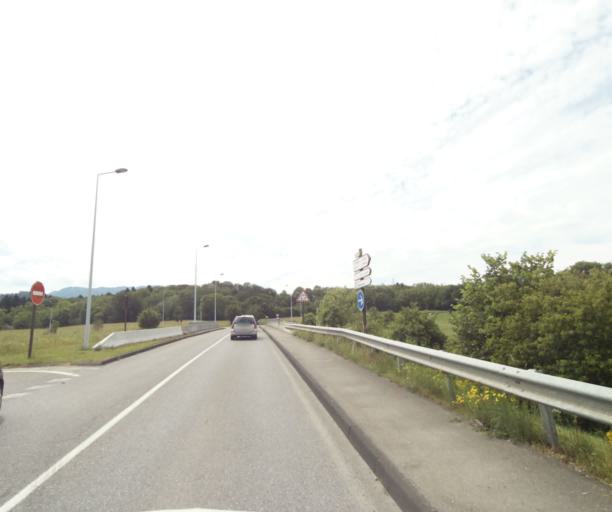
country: FR
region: Rhone-Alpes
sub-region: Departement de la Haute-Savoie
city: Margencel
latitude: 46.3487
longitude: 6.4413
